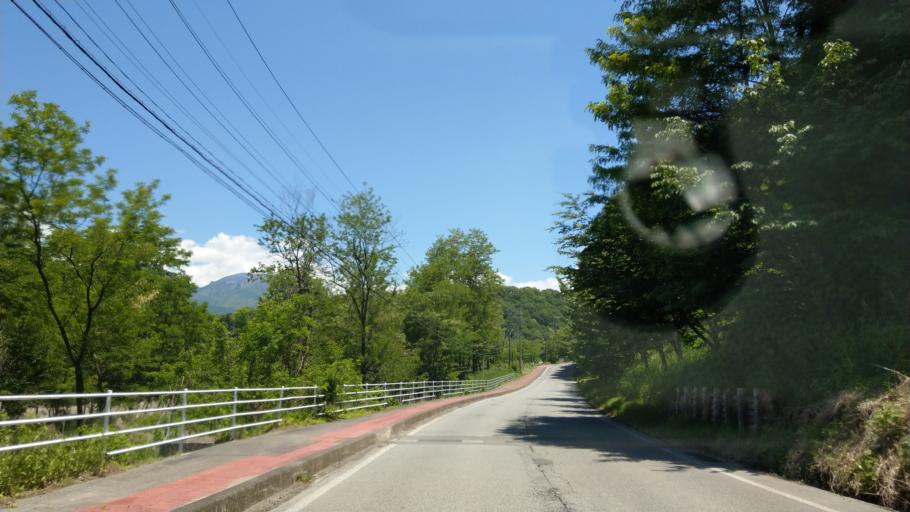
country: JP
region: Nagano
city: Komoro
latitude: 36.3254
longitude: 138.4079
